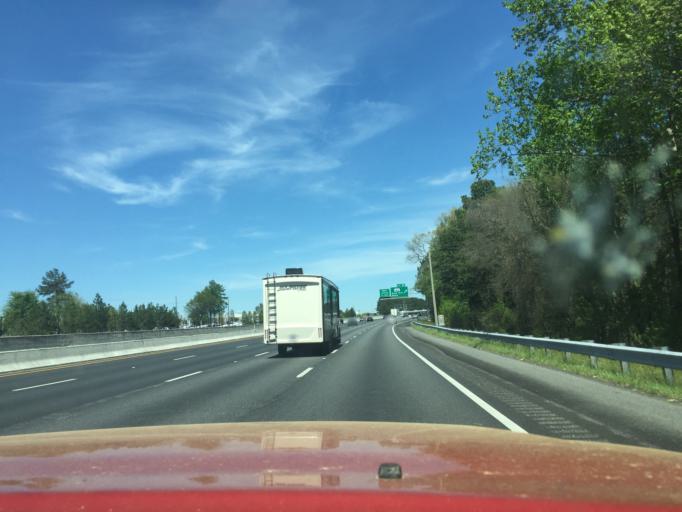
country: US
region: South Carolina
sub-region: York County
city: Fort Mill
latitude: 35.0556
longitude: -80.9578
